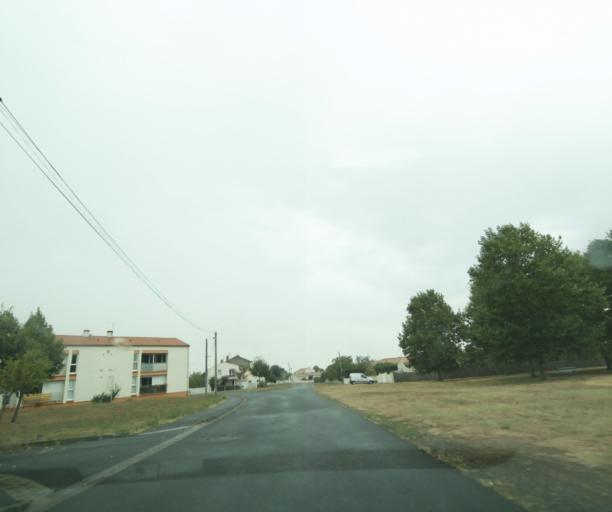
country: FR
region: Poitou-Charentes
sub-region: Departement de la Charente-Maritime
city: Tonnay-Charente
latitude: 45.9442
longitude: -0.9042
